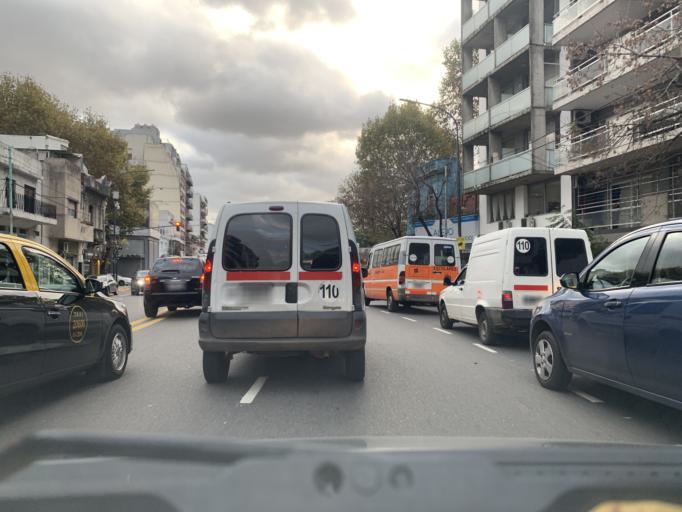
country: AR
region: Buenos Aires F.D.
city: Colegiales
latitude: -34.5784
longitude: -58.4578
